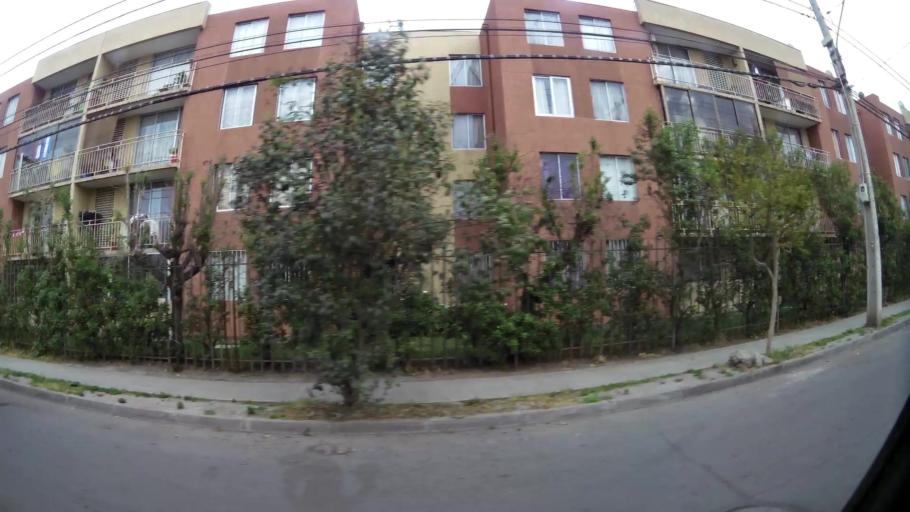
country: CL
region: Santiago Metropolitan
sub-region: Provincia de Santiago
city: Lo Prado
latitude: -33.4871
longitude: -70.7403
